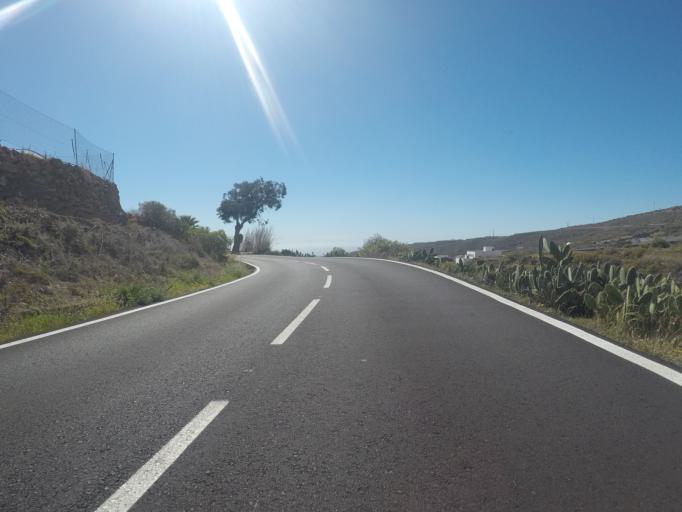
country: ES
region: Canary Islands
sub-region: Provincia de Santa Cruz de Tenerife
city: Lomo de Arico
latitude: 28.1717
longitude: -16.4979
